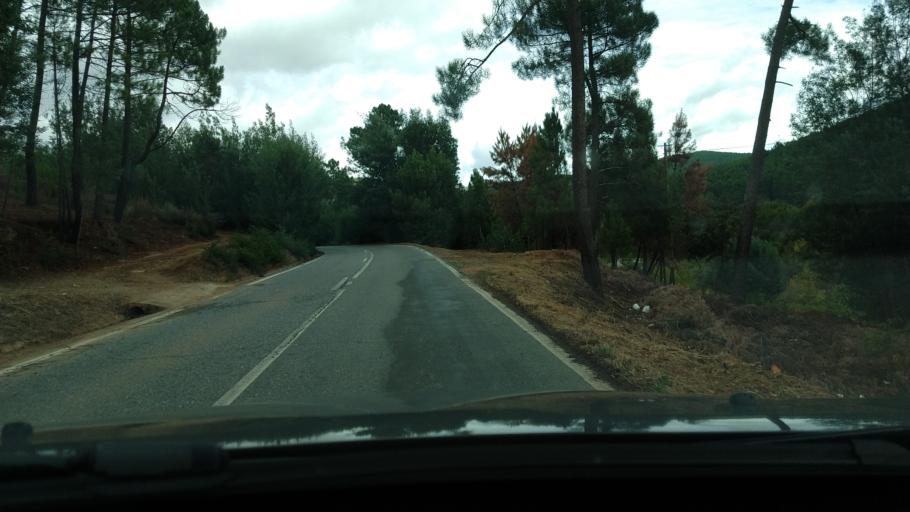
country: PT
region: Castelo Branco
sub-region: Covilha
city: Covilha
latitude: 40.2232
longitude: -7.6119
